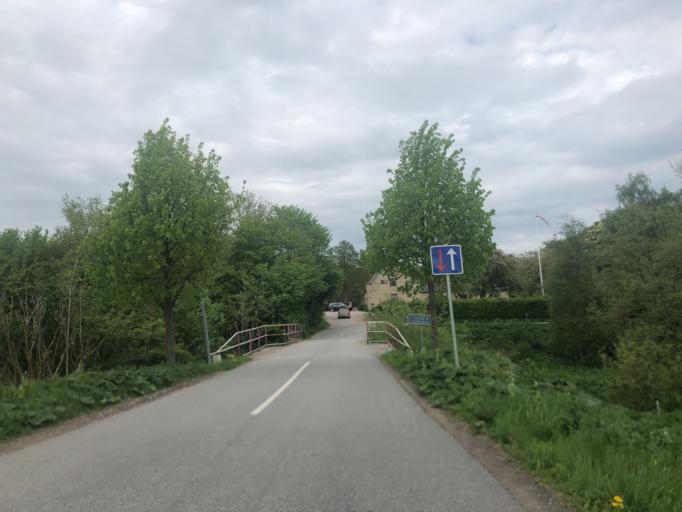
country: DK
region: Zealand
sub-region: Koge Kommune
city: Ejby
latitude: 55.4689
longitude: 12.1106
